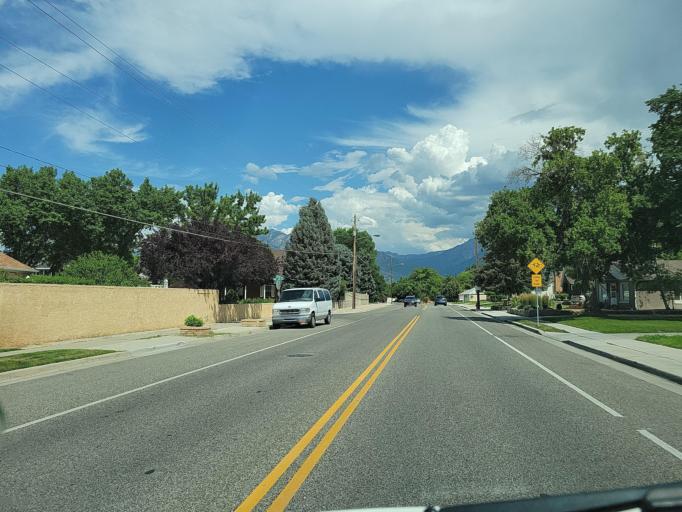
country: US
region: Utah
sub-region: Salt Lake County
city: Murray
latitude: 40.6420
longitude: -111.8810
